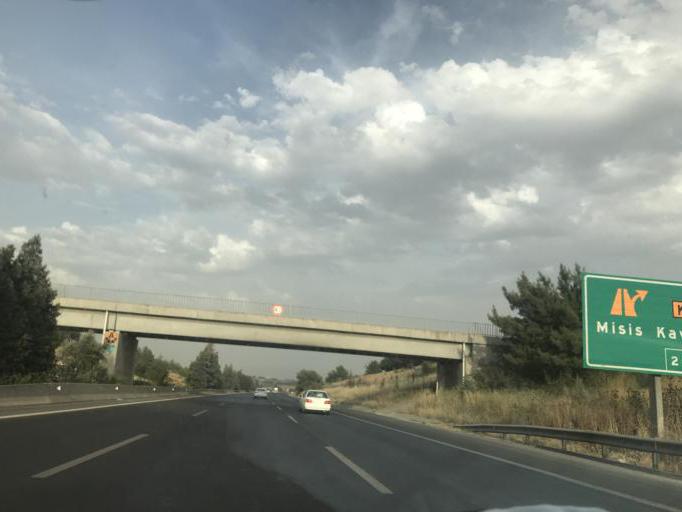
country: TR
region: Adana
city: Yakapinar
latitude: 36.9990
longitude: 35.5625
